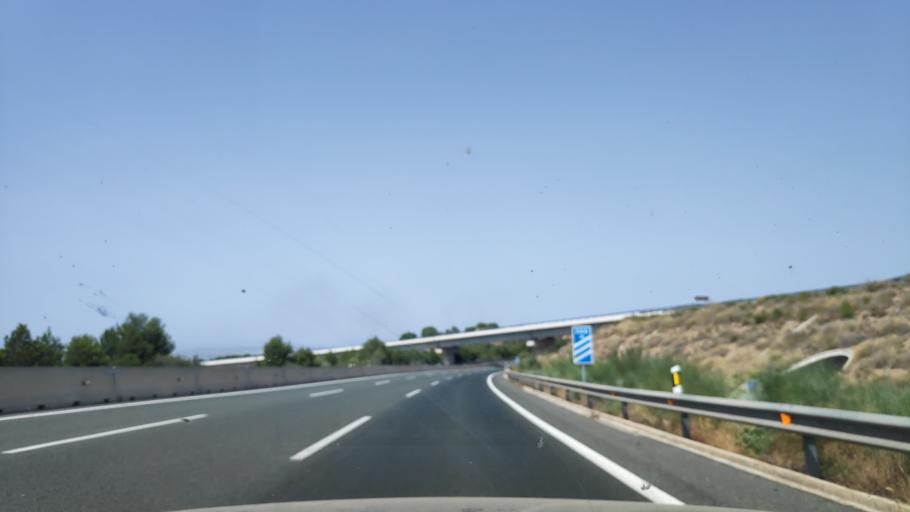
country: ES
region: Murcia
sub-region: Murcia
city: Alcantarilla
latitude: 37.9170
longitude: -1.1643
